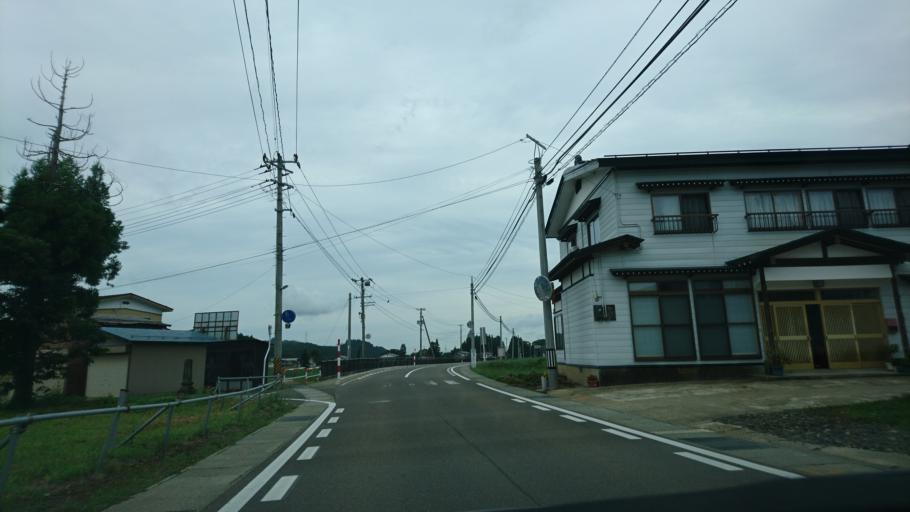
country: JP
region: Akita
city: Yuzawa
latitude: 39.1696
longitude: 140.5586
